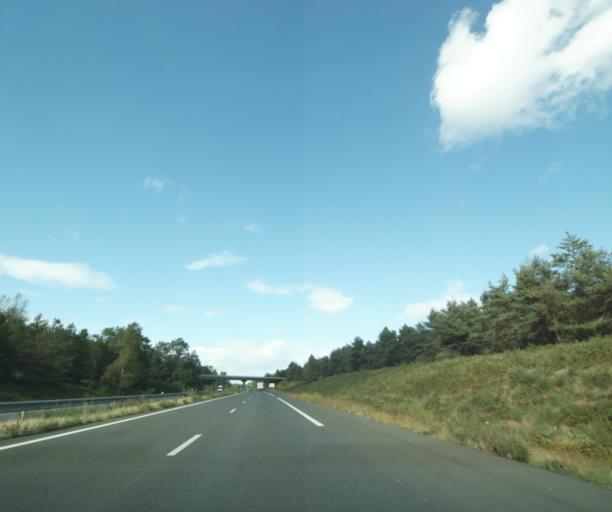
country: FR
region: Centre
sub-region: Departement du Loiret
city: Saint-Hilaire-Saint-Mesmin
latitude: 47.8208
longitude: 1.8586
